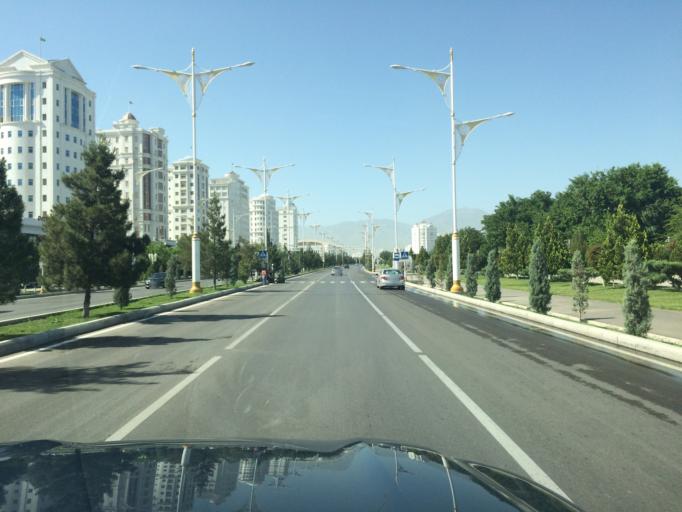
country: TM
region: Ahal
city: Ashgabat
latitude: 37.9233
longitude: 58.3755
